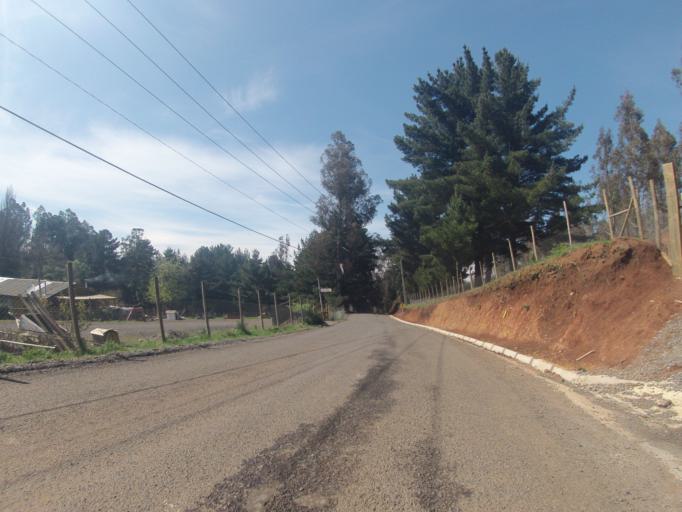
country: CL
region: Araucania
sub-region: Provincia de Cautin
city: Temuco
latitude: -38.6864
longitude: -72.5590
